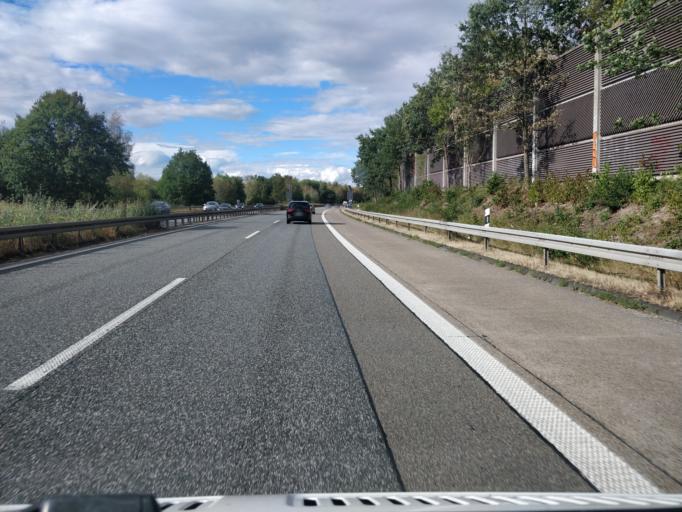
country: DE
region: North Rhine-Westphalia
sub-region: Regierungsbezirk Koln
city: Bonn
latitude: 50.6875
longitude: 7.0568
